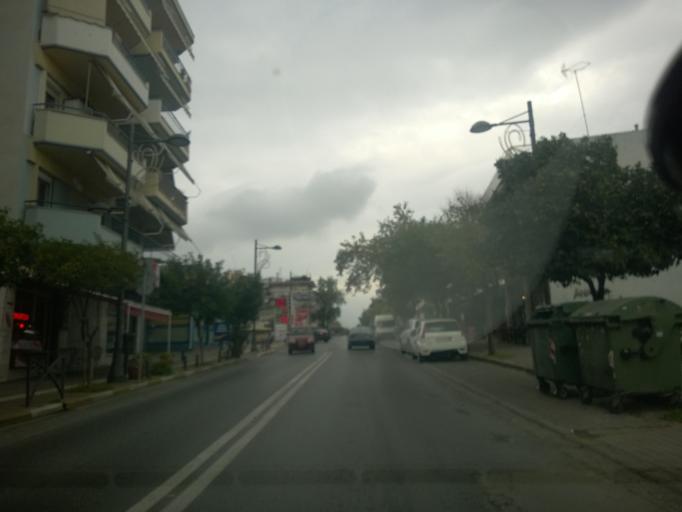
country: GR
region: Central Macedonia
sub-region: Nomos Thessalonikis
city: Stavroupoli
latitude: 40.6685
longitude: 22.9329
